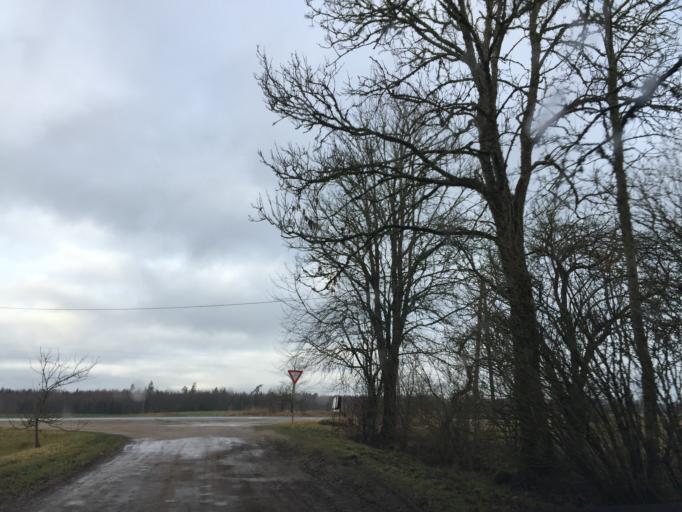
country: LV
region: Vainode
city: Vainode
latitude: 56.6155
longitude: 21.7946
